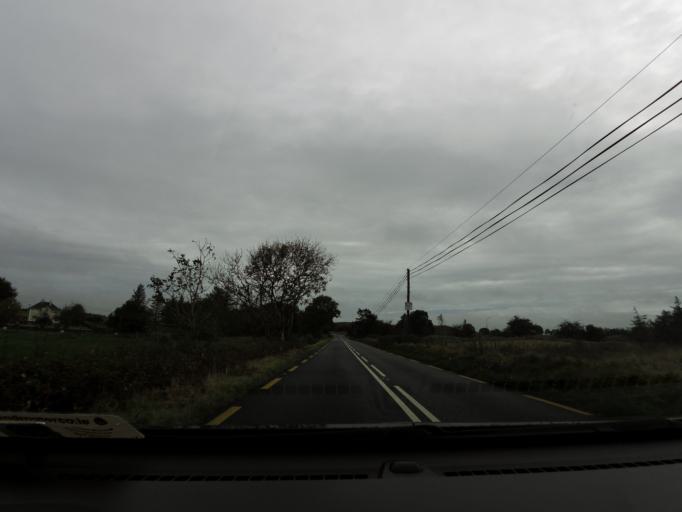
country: IE
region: Connaught
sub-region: County Galway
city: Tuam
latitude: 53.6031
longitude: -8.7586
